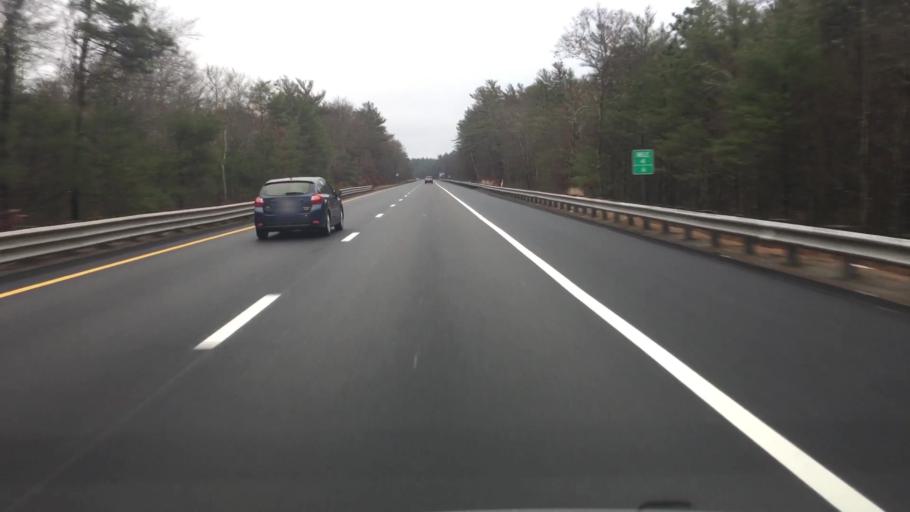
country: US
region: Massachusetts
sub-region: Plymouth County
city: West Wareham
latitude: 41.8210
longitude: -70.8044
